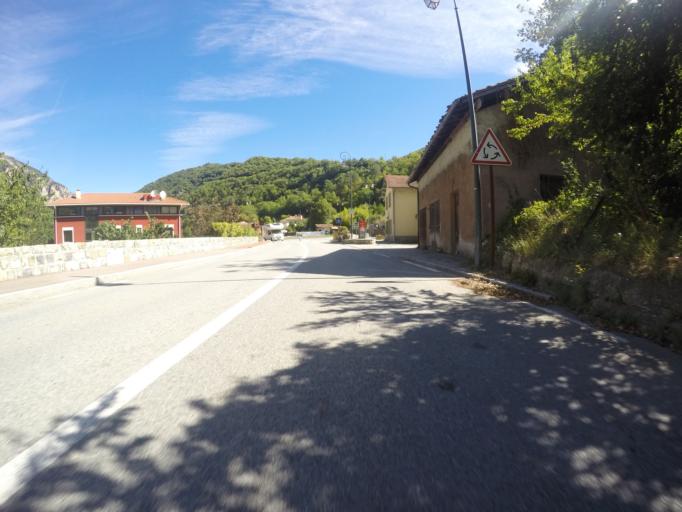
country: FR
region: Provence-Alpes-Cote d'Azur
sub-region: Departement des Alpes-Maritimes
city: Gilette
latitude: 43.9758
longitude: 7.1398
